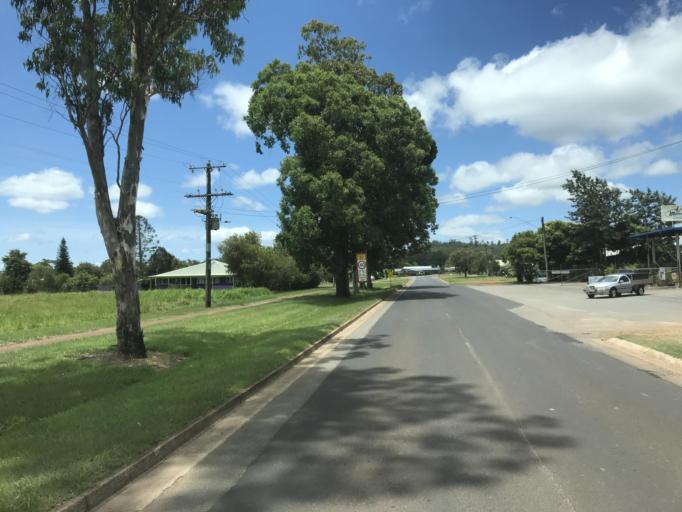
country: AU
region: Queensland
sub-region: Tablelands
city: Ravenshoe
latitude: -17.6131
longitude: 145.4868
